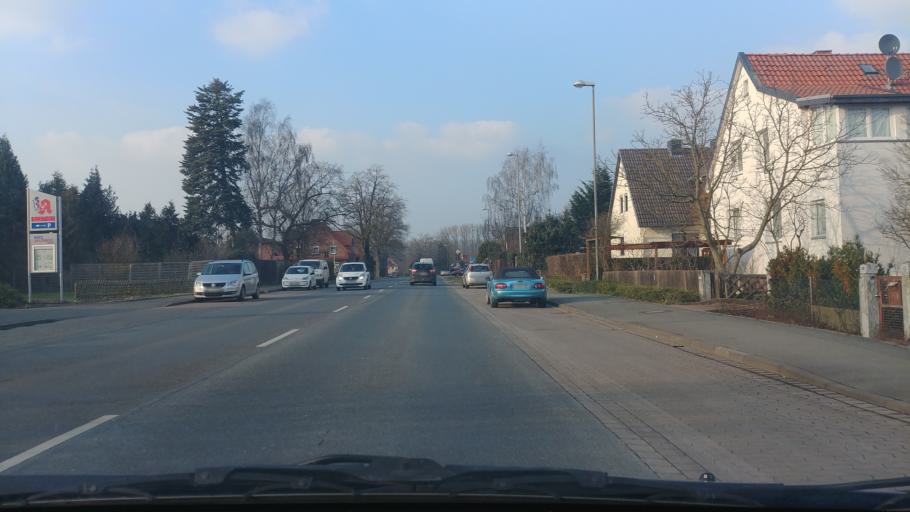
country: DE
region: Lower Saxony
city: Hemmingen
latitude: 52.3059
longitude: 9.7370
